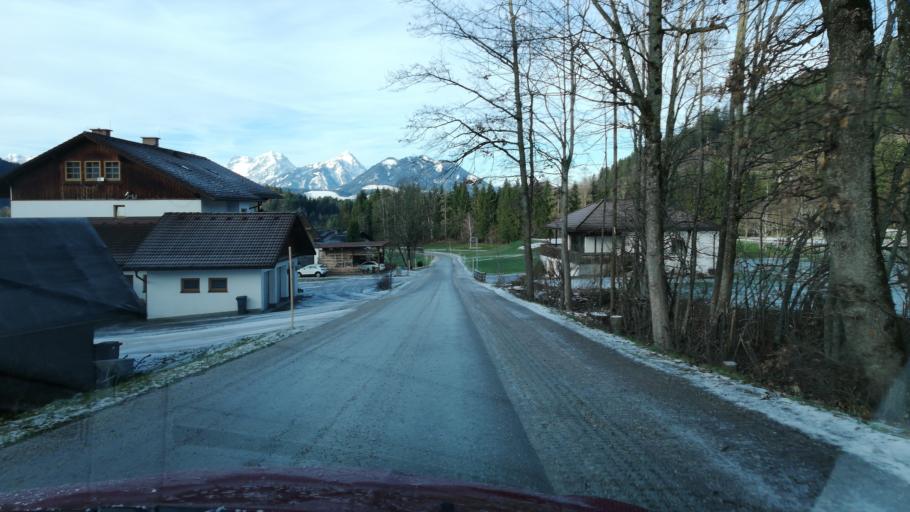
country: AT
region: Upper Austria
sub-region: Politischer Bezirk Kirchdorf an der Krems
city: Rossleithen
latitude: 47.7163
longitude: 14.3587
